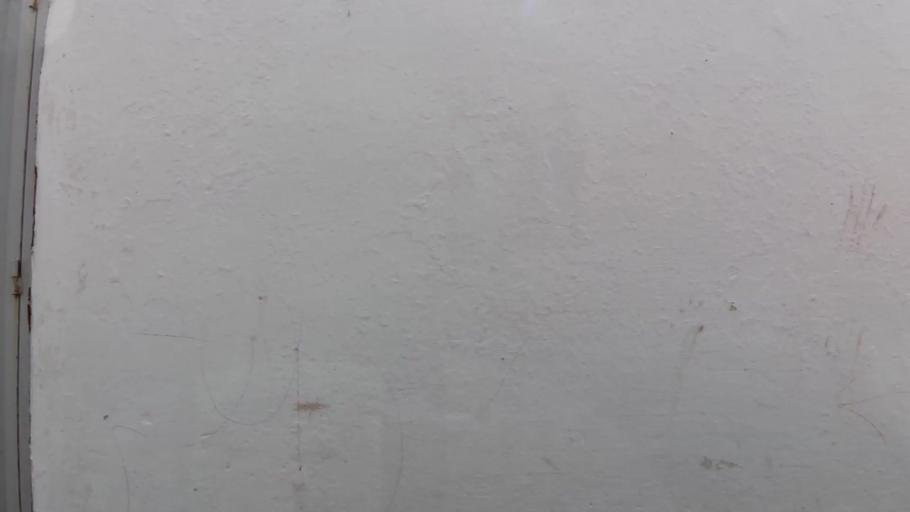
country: MA
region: Tanger-Tetouan
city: Tetouan
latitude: 35.5785
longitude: -5.3989
